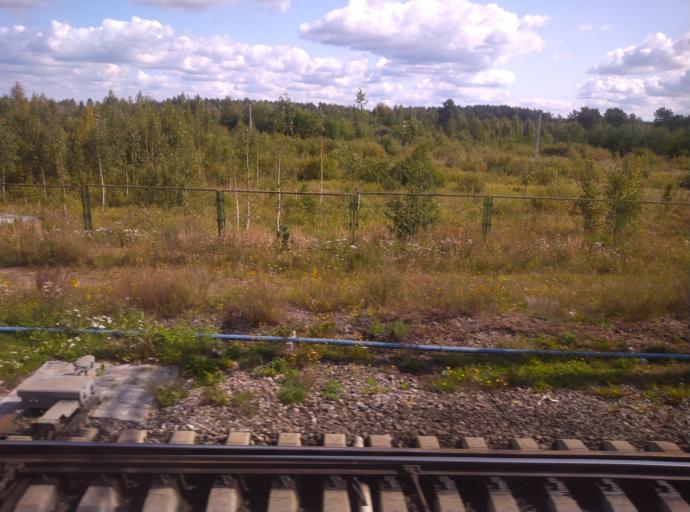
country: RU
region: Leningrad
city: Ul'yanovka
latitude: 59.6262
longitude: 30.7694
